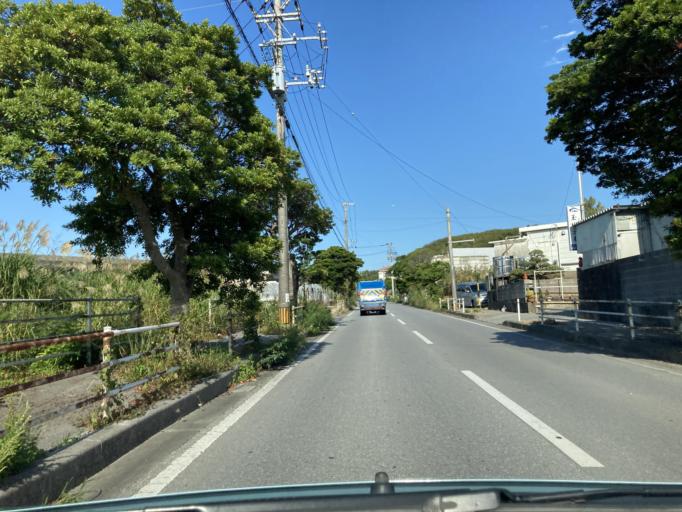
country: JP
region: Okinawa
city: Tomigusuku
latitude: 26.1731
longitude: 127.7043
